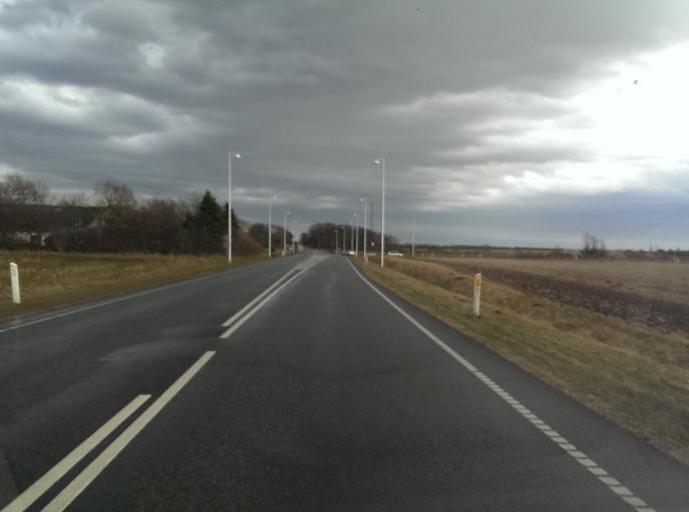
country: DK
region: South Denmark
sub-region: Esbjerg Kommune
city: Tjaereborg
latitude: 55.4960
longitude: 8.6208
